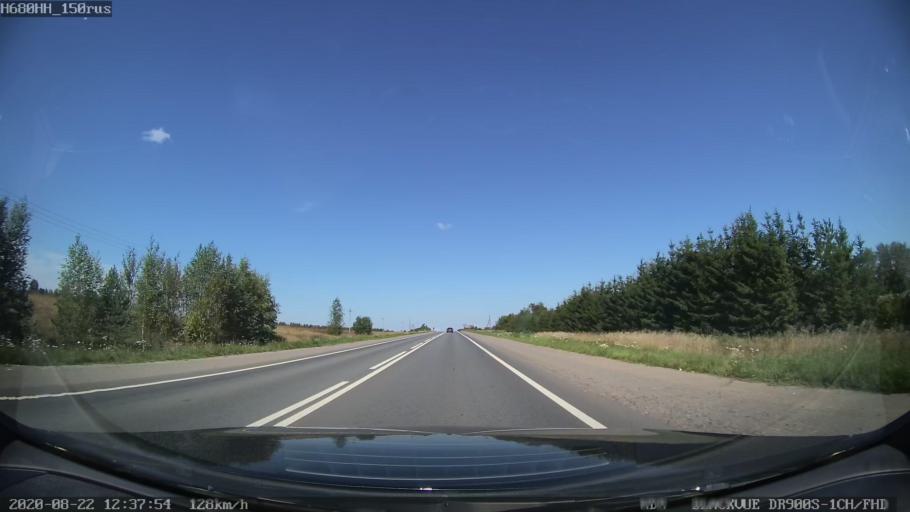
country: RU
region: Tverskaya
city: Rameshki
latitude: 57.3049
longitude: 36.0892
